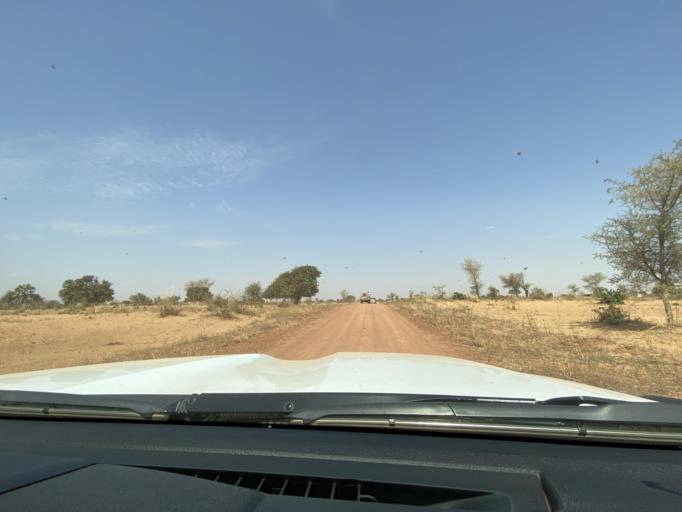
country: NE
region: Dosso
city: Birnin Gaoure
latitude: 13.2319
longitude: 2.8691
